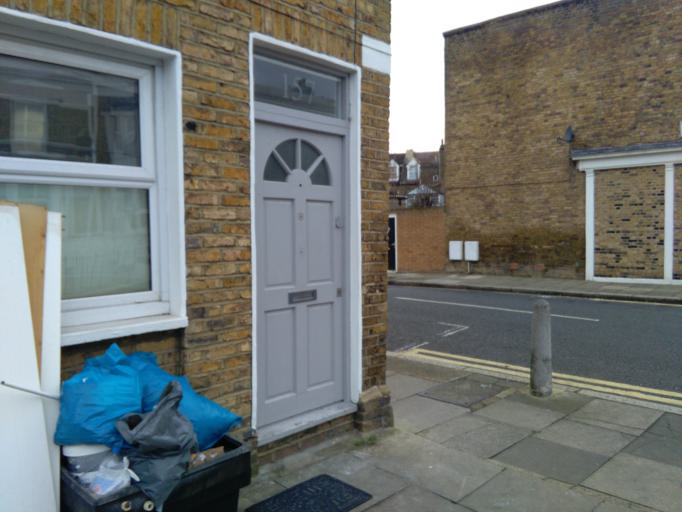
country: GB
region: England
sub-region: Greater London
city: Brixton Hill
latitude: 51.4627
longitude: -0.1217
